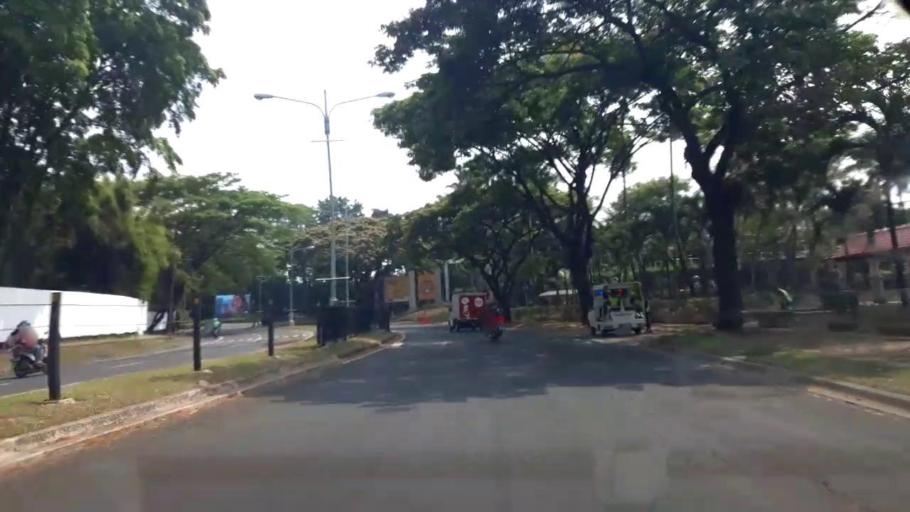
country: ID
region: Banten
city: Tangerang
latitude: -6.2263
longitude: 106.6046
